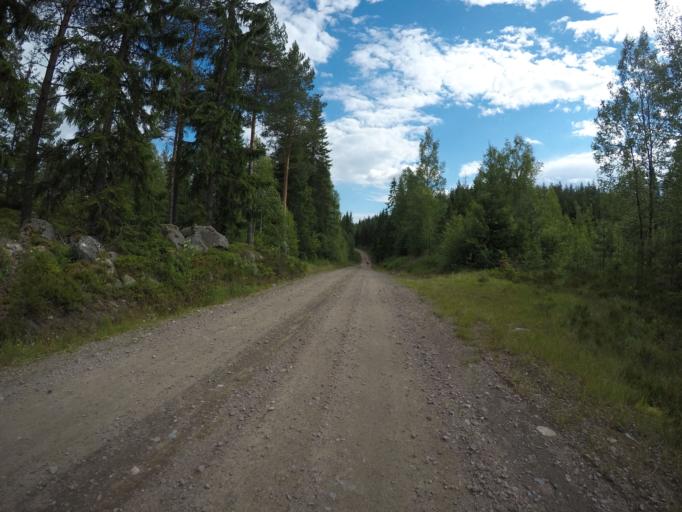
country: SE
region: Vaermland
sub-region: Filipstads Kommun
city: Lesjofors
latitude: 60.0676
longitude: 14.4342
